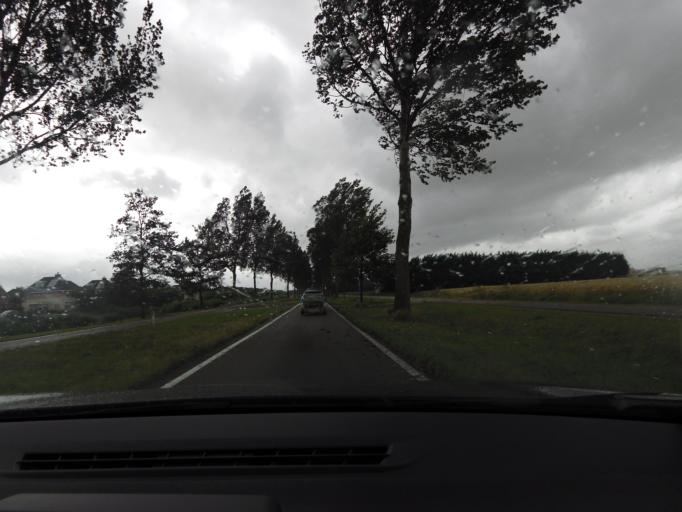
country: NL
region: South Holland
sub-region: Gemeente Hellevoetsluis
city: Nieuwenhoorn
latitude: 51.8475
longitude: 4.1661
